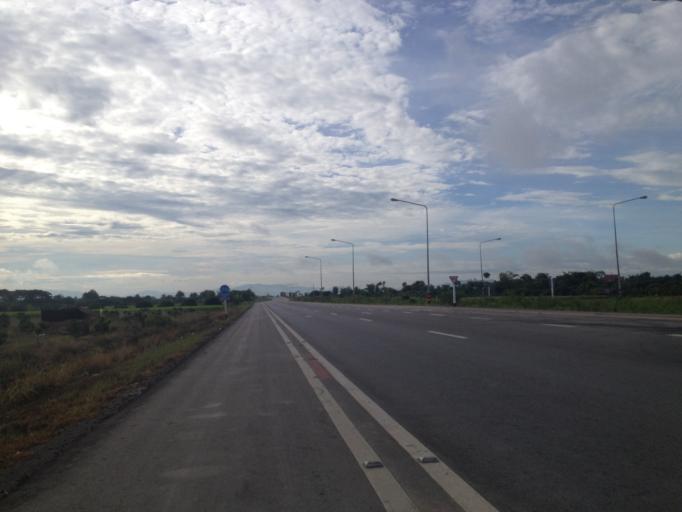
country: TH
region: Chiang Mai
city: San Pa Tong
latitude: 18.5863
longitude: 98.8397
